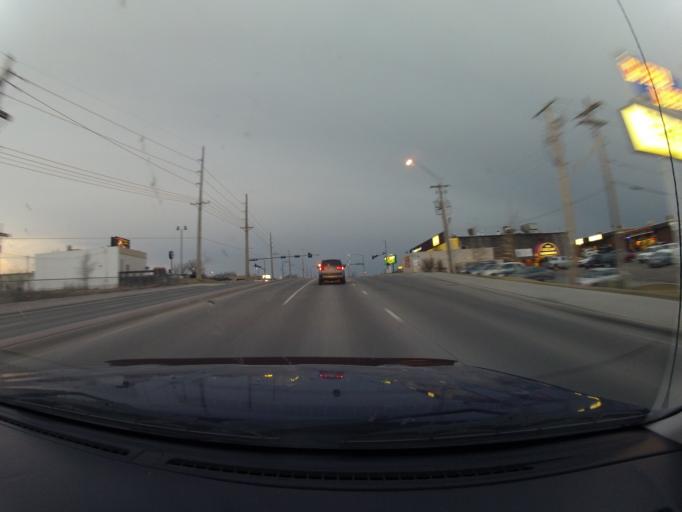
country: US
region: Nebraska
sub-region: Buffalo County
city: Kearney
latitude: 40.7139
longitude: -99.0825
